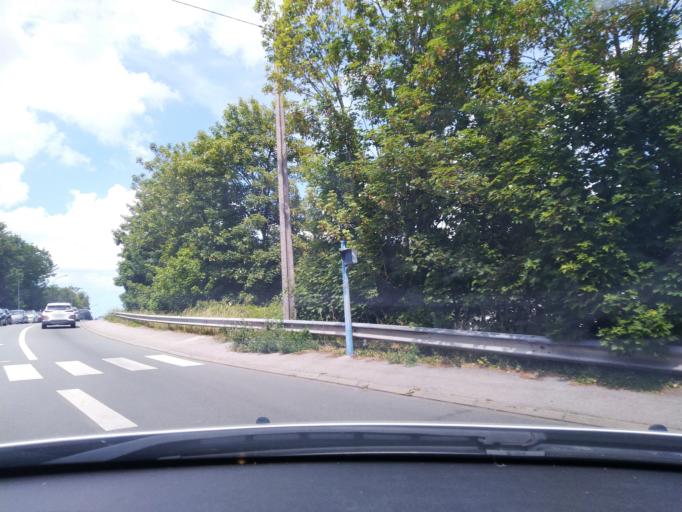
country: FR
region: Nord-Pas-de-Calais
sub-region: Departement du Pas-de-Calais
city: Saint-Etienne-au-Mont
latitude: 50.6786
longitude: 1.6335
